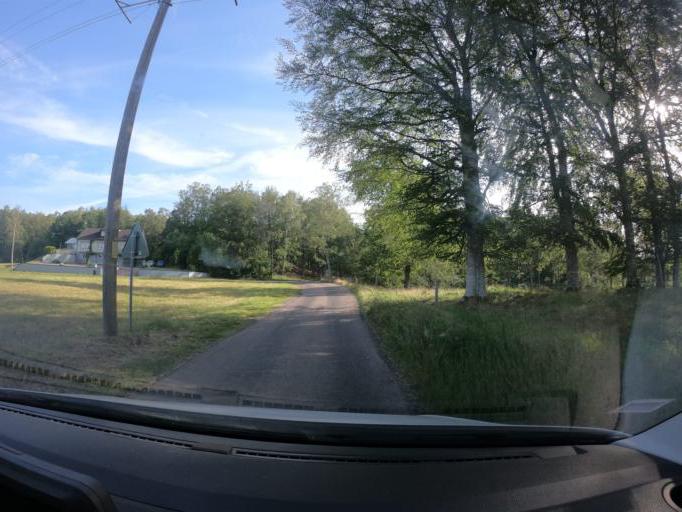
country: SE
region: Skane
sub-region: Angelholms Kommun
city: Munka-Ljungby
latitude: 56.3302
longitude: 12.9761
